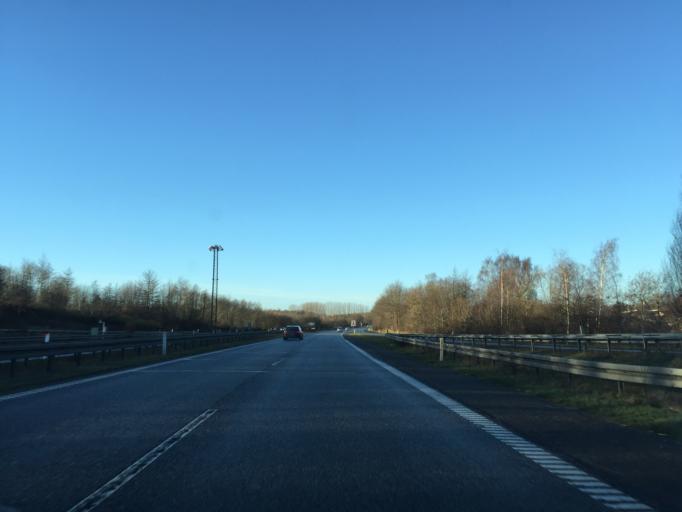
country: DK
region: South Denmark
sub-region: Odense Kommune
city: Odense
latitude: 55.3534
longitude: 10.3734
